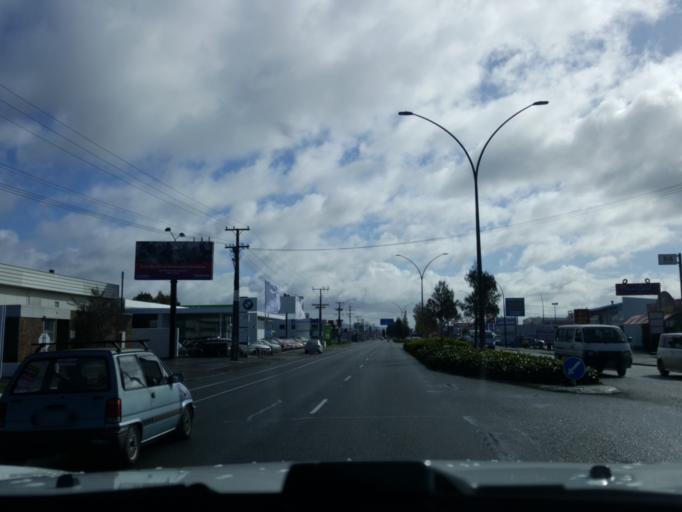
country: NZ
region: Waikato
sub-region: Hamilton City
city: Hamilton
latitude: -37.7609
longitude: 175.2492
